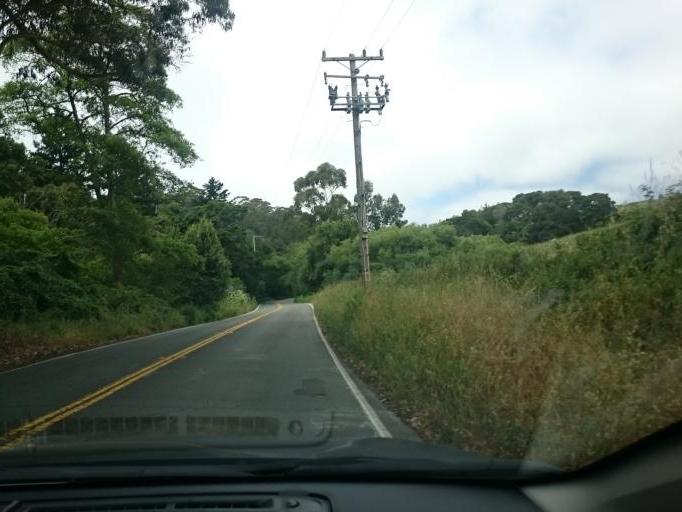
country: US
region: California
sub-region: Marin County
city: Bolinas
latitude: 37.9364
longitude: -122.7010
